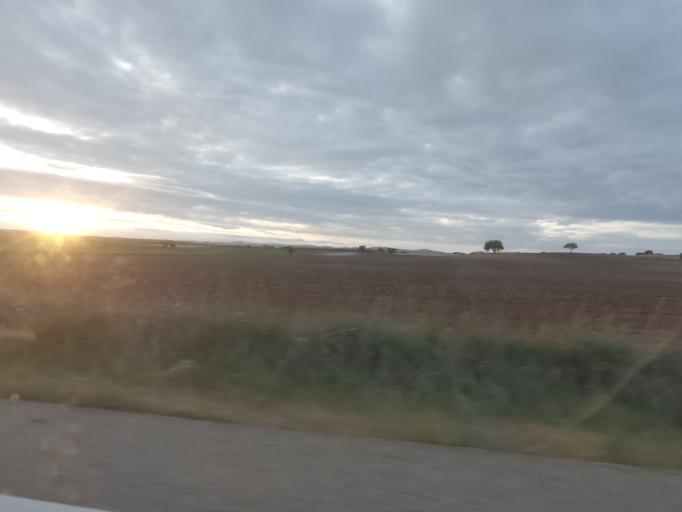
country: ES
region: Extremadura
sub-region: Provincia de Badajoz
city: Villar del Rey
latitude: 39.0568
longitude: -6.7904
